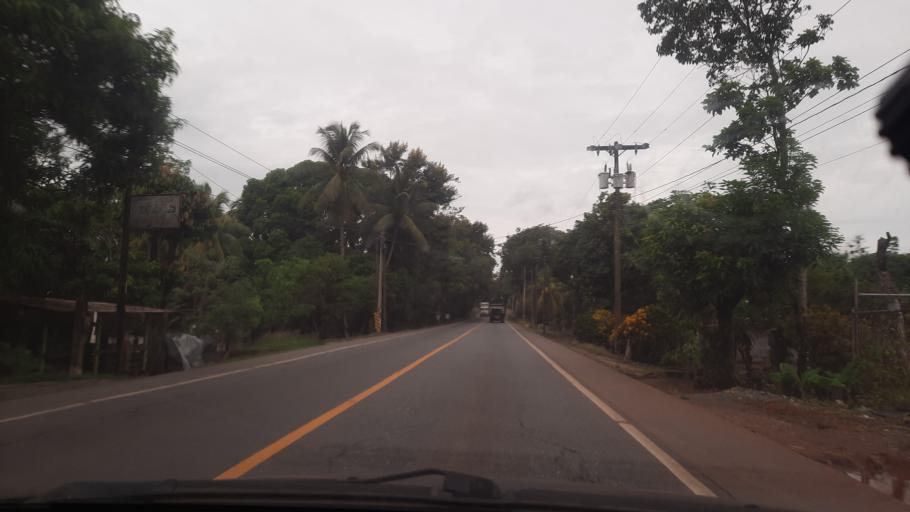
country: GT
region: Izabal
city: Morales
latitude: 15.4411
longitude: -88.9515
